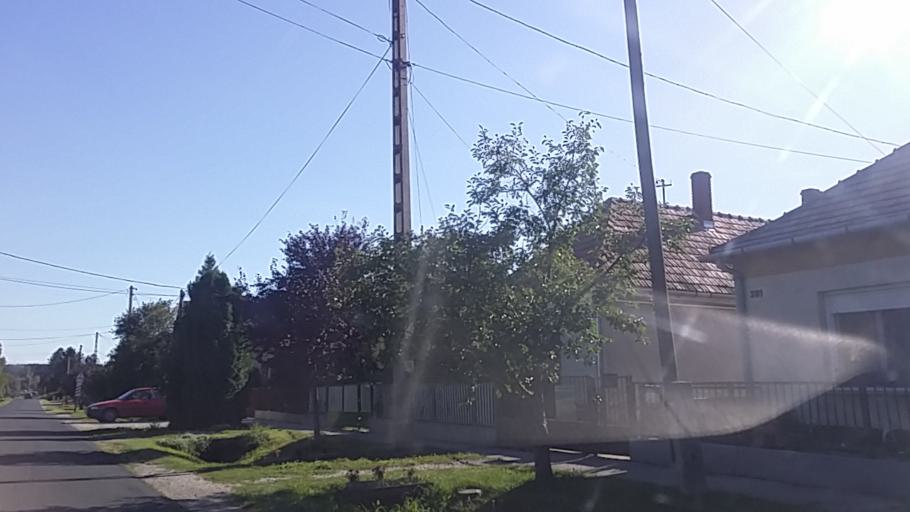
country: HU
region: Zala
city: Sarmellek
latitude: 46.7055
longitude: 17.1679
